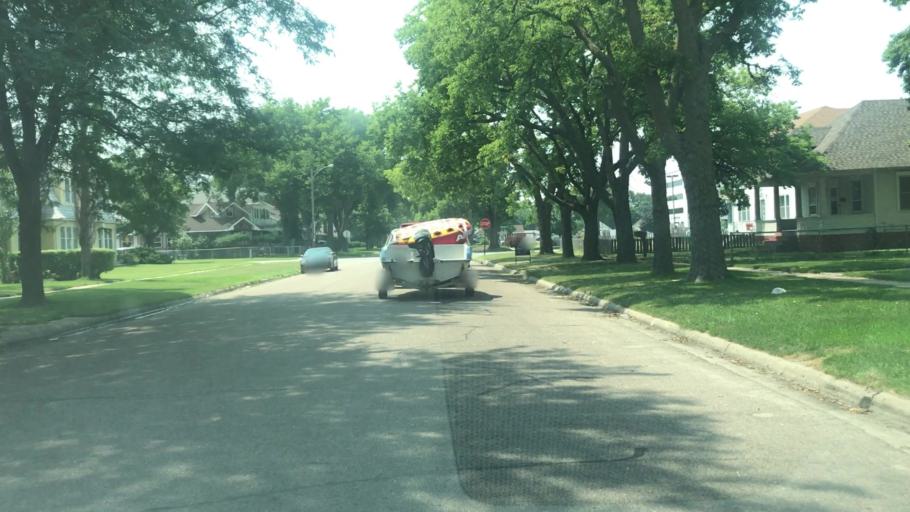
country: US
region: Nebraska
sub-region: Hall County
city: Grand Island
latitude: 40.9173
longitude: -98.3555
